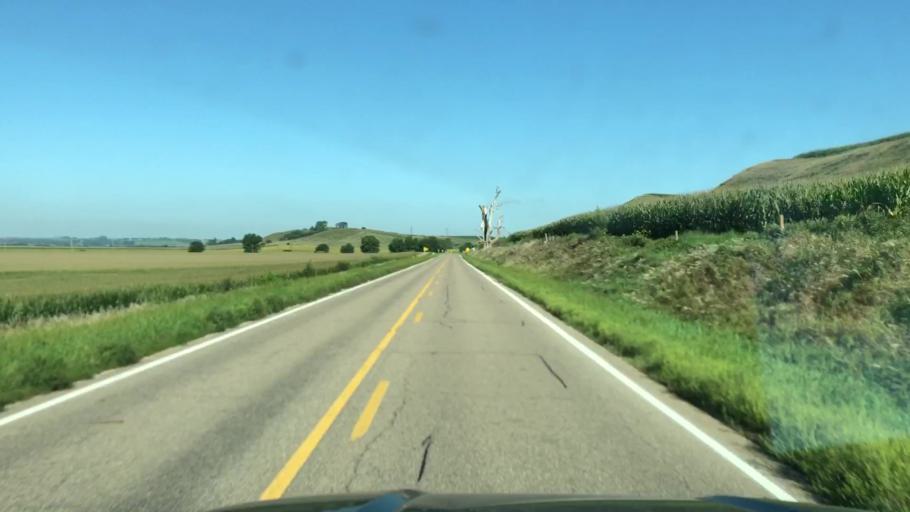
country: US
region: Iowa
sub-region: Woodbury County
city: Sergeant Bluff
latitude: 42.4059
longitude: -96.2506
